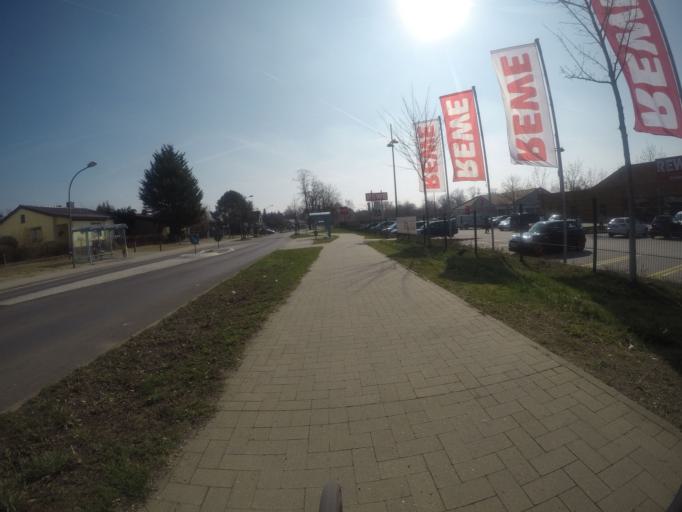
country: DE
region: Brandenburg
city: Konigs Wusterhausen
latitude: 52.3046
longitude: 13.6498
